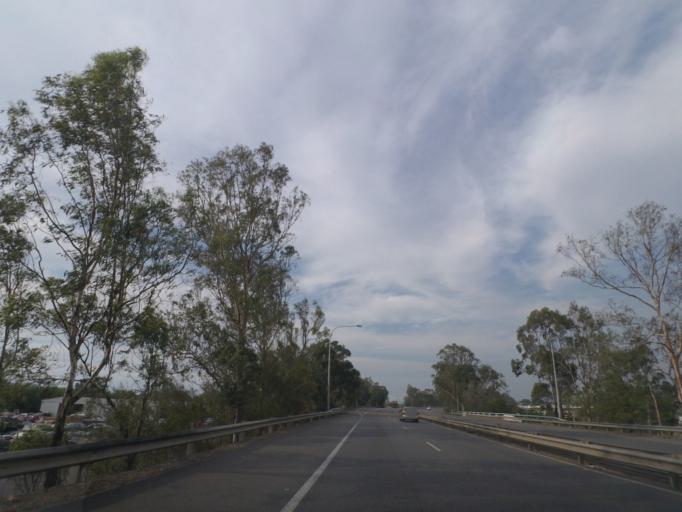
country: AU
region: Queensland
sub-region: Brisbane
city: Rocklea
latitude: -27.5469
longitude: 153.0099
